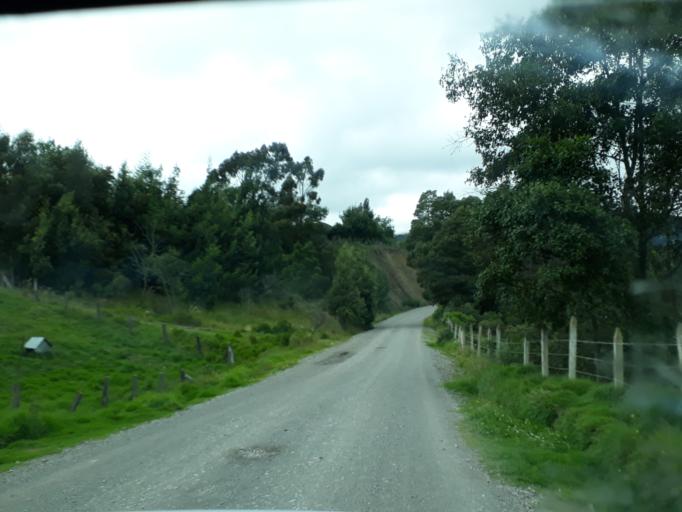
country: CO
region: Cundinamarca
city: La Mesa
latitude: 5.2878
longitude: -73.9037
